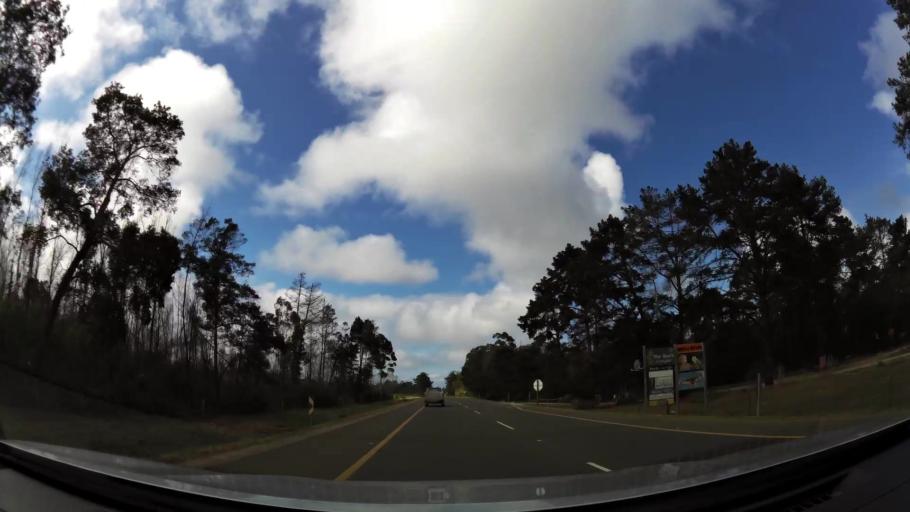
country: ZA
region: Western Cape
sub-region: Eden District Municipality
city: Plettenberg Bay
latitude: -34.0443
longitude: 23.2996
